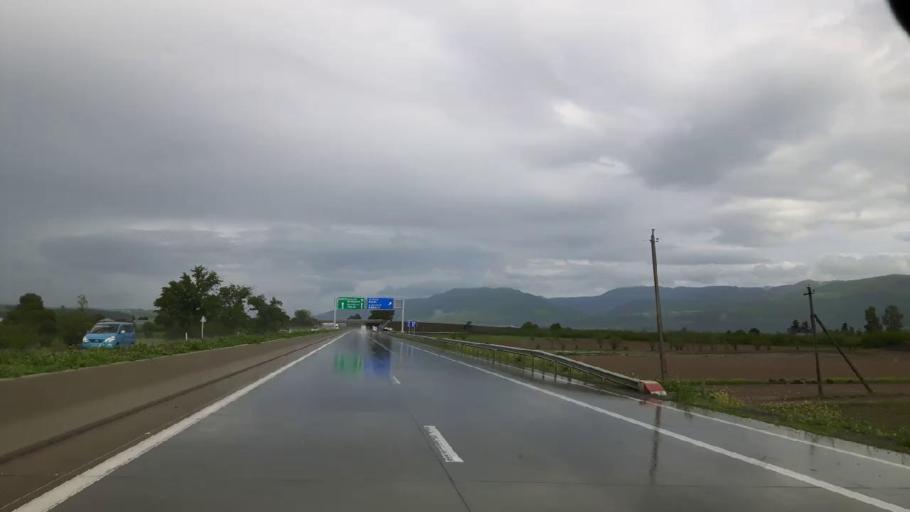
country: GE
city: Agara
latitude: 42.0336
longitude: 43.9445
